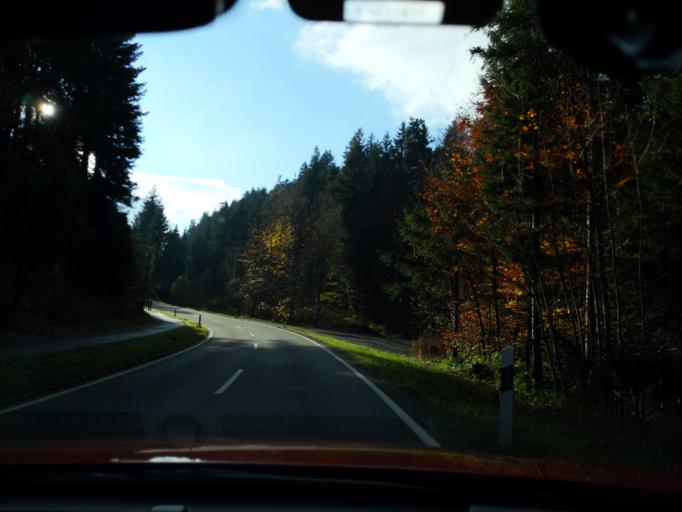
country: AT
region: Vorarlberg
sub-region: Politischer Bezirk Bregenz
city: Moggers
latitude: 47.5761
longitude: 9.8308
